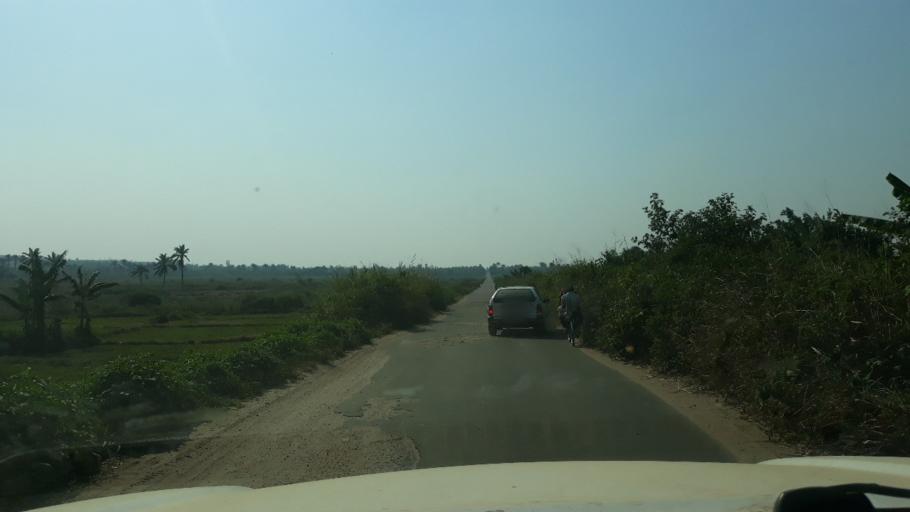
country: BI
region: Cibitoke
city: Cibitoke
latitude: -2.9752
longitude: 29.0873
